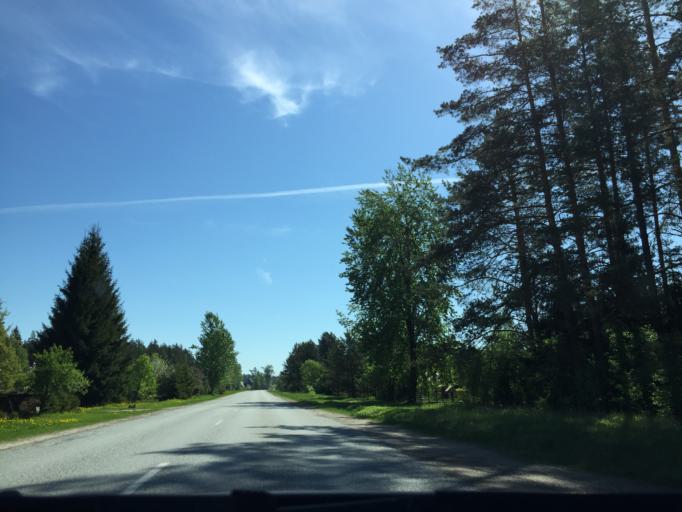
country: LV
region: Incukalns
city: Vangazi
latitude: 57.0106
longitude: 24.5403
